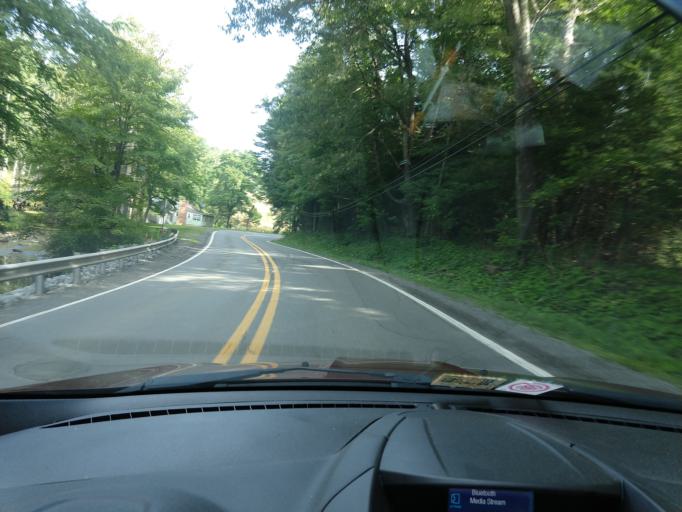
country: US
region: West Virginia
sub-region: Nicholas County
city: Richwood
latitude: 38.1625
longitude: -80.6908
